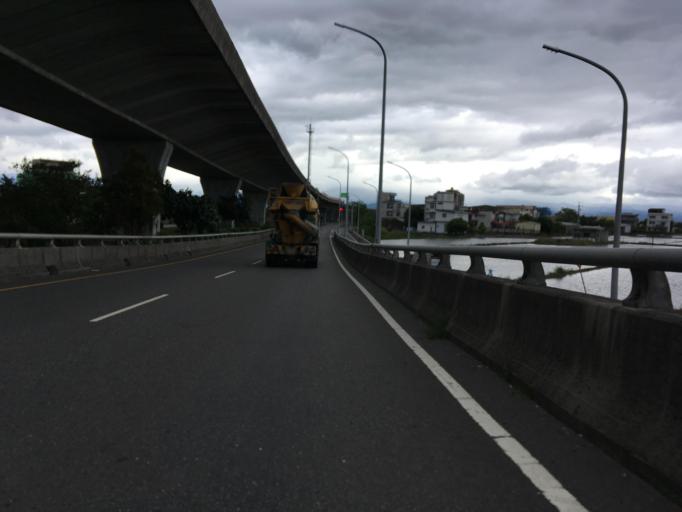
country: TW
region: Taiwan
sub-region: Yilan
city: Yilan
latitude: 24.6637
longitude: 121.7995
